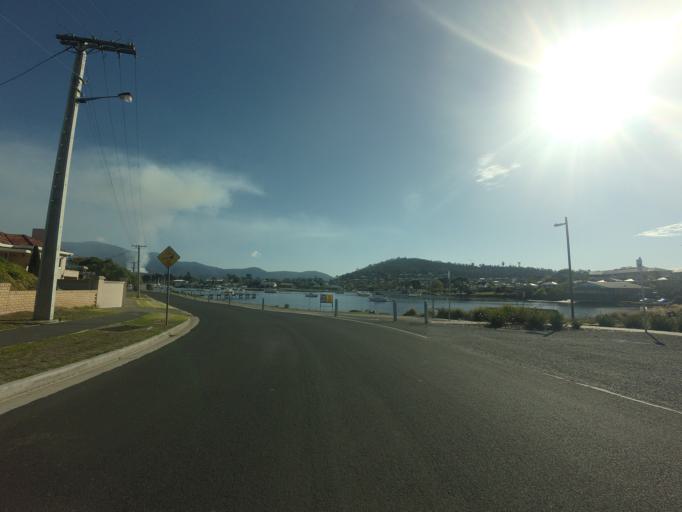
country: AU
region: Tasmania
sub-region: Clarence
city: Lindisfarne
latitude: -42.8499
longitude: 147.3593
